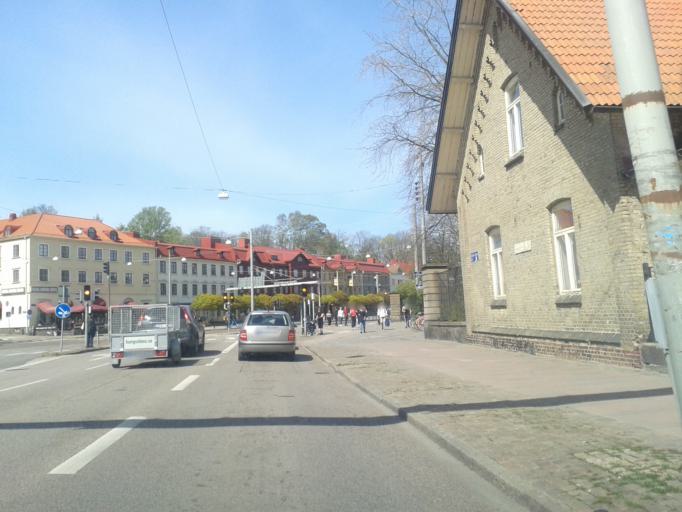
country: SE
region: Vaestra Goetaland
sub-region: Goteborg
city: Goeteborg
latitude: 57.7151
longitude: 12.0046
